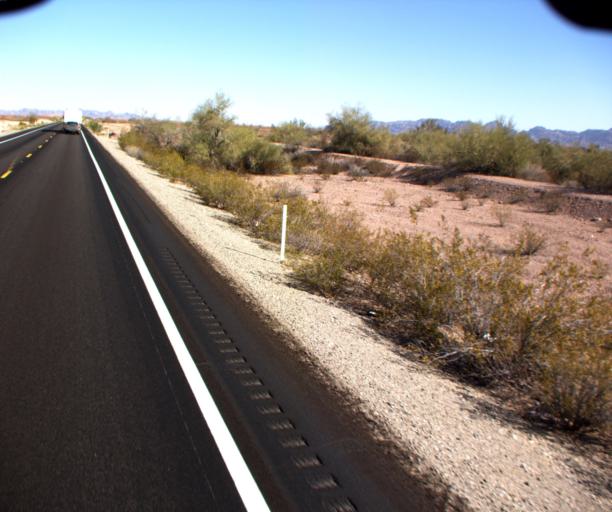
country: US
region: Arizona
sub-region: Yuma County
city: Wellton
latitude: 33.0602
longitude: -114.2926
